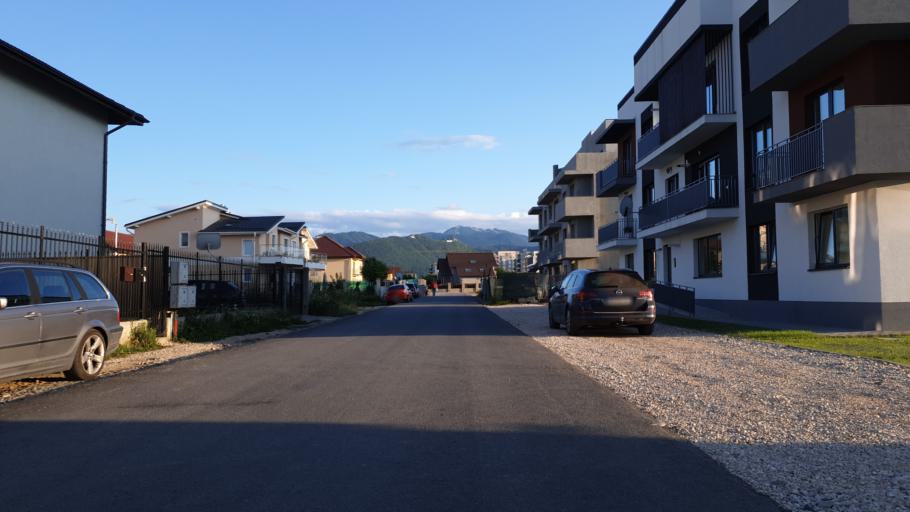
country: RO
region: Brasov
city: Brasov
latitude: 45.6784
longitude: 25.6089
